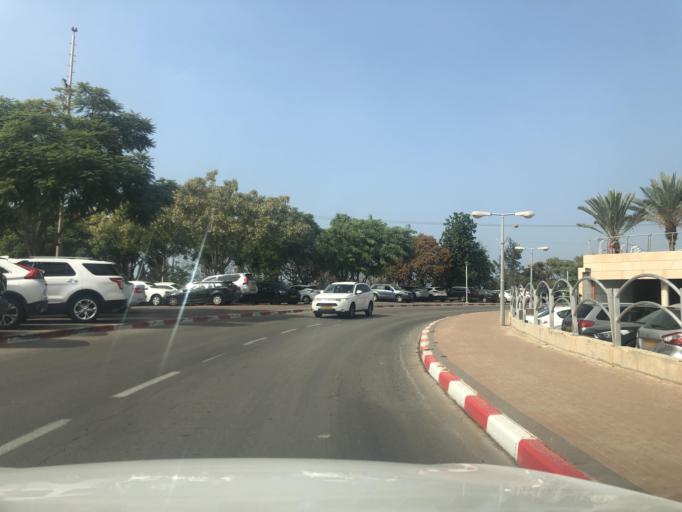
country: IL
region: Tel Aviv
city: Or Yehuda
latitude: 32.0443
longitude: 34.8413
